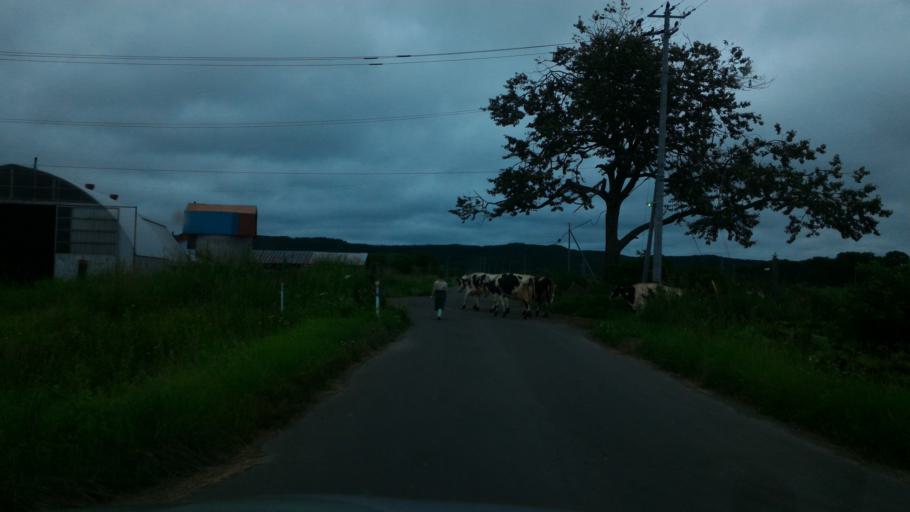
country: JP
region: Hokkaido
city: Kushiro
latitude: 43.0678
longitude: 144.1907
